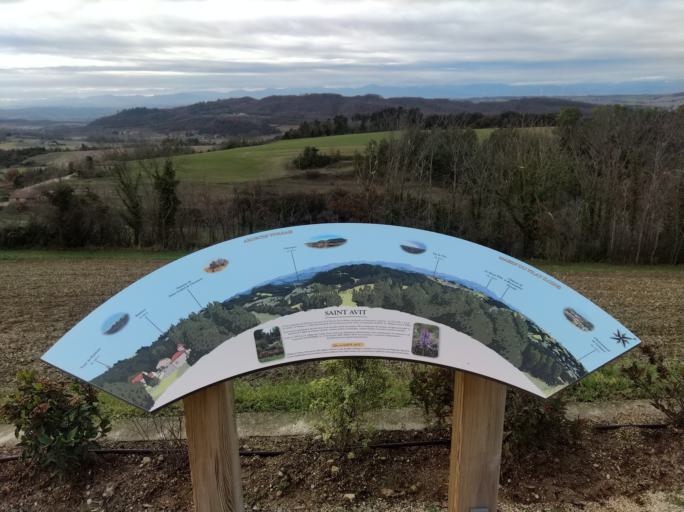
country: FR
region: Rhone-Alpes
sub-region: Departement de la Drome
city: Chateauneuf-de-Galaure
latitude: 45.1970
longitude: 4.9686
